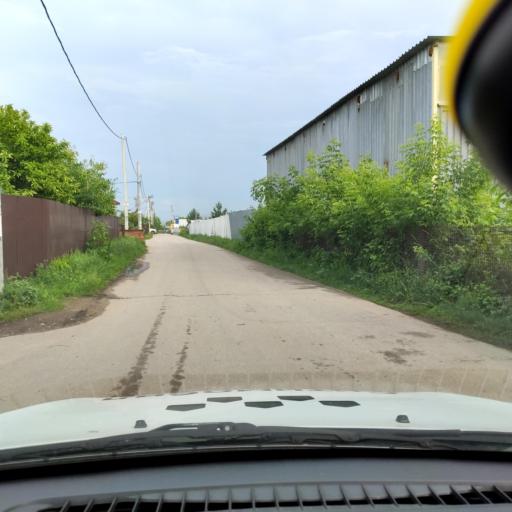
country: RU
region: Samara
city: Podstepki
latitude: 53.5762
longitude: 49.0763
